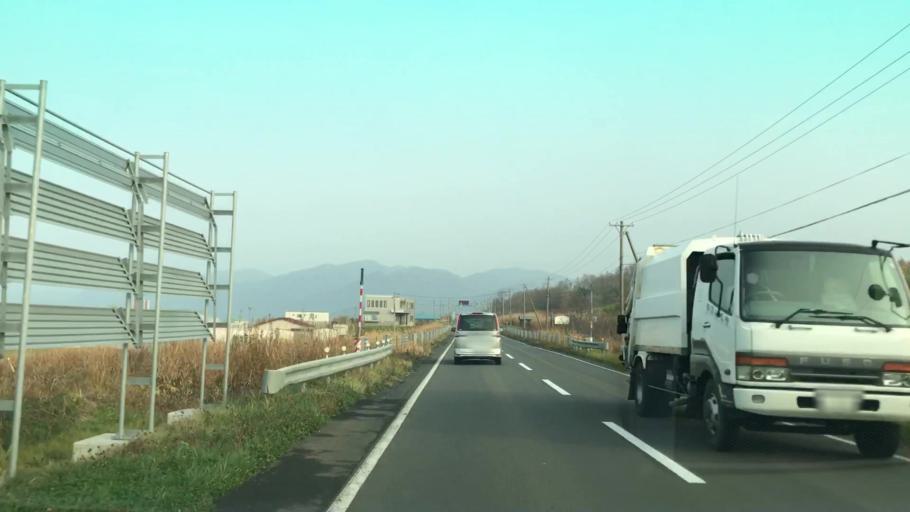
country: JP
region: Hokkaido
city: Ishikari
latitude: 43.3739
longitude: 141.4273
